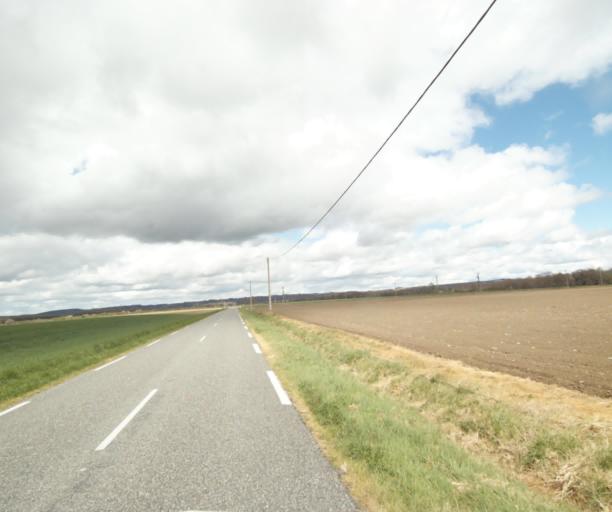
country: FR
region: Midi-Pyrenees
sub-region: Departement de l'Ariege
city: Mazeres
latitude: 43.2458
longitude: 1.6370
